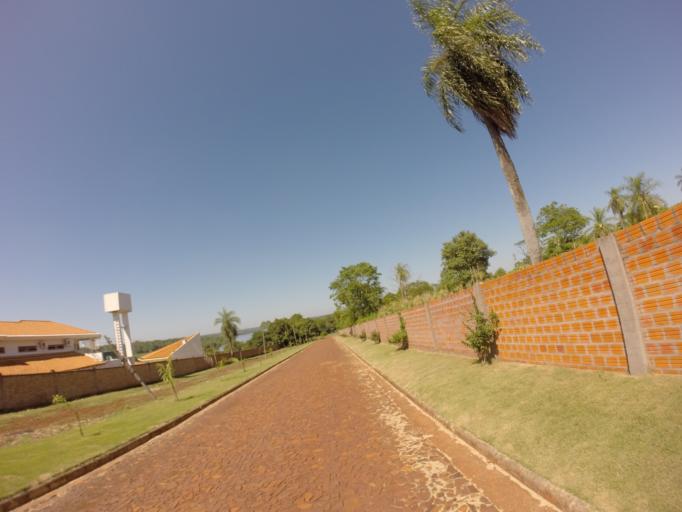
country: PY
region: Alto Parana
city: Ciudad del Este
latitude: -25.4381
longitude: -54.6472
